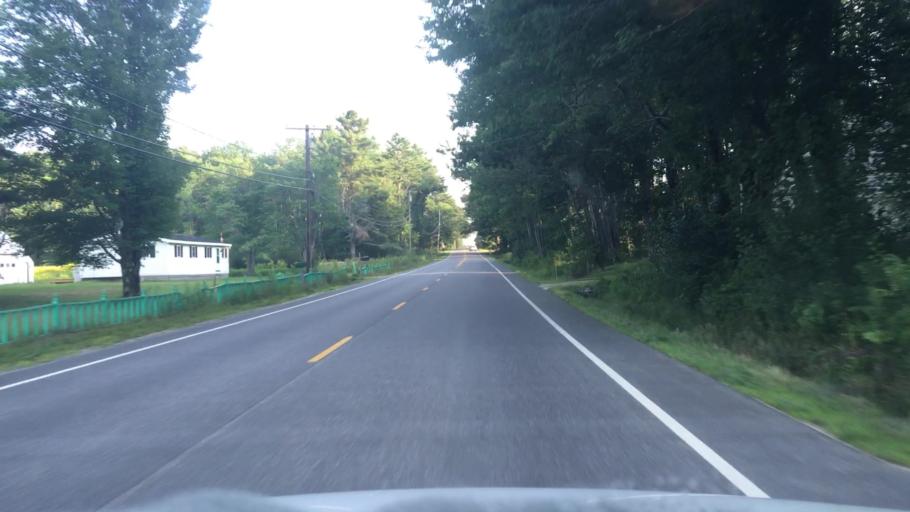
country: US
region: Maine
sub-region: Cumberland County
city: Freeport
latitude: 43.8903
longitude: -70.0943
